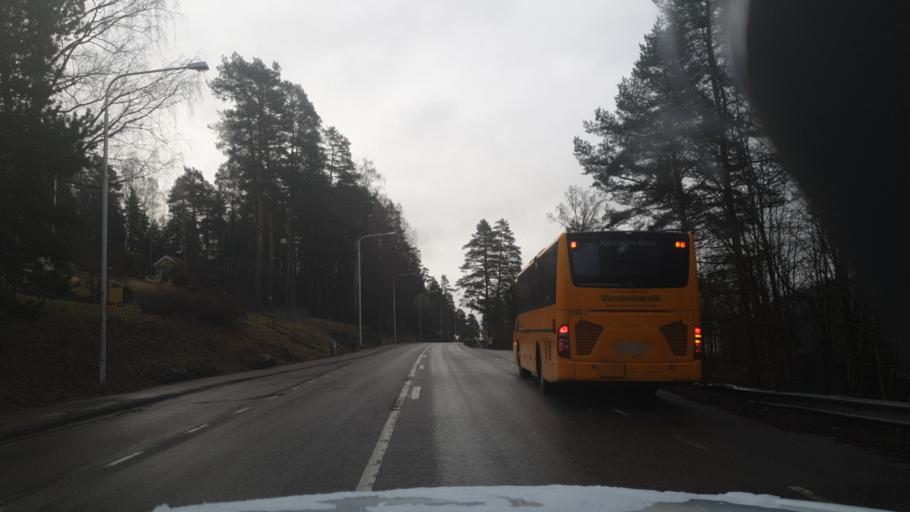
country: SE
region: Vaermland
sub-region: Arvika Kommun
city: Arvika
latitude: 59.6718
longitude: 12.4740
